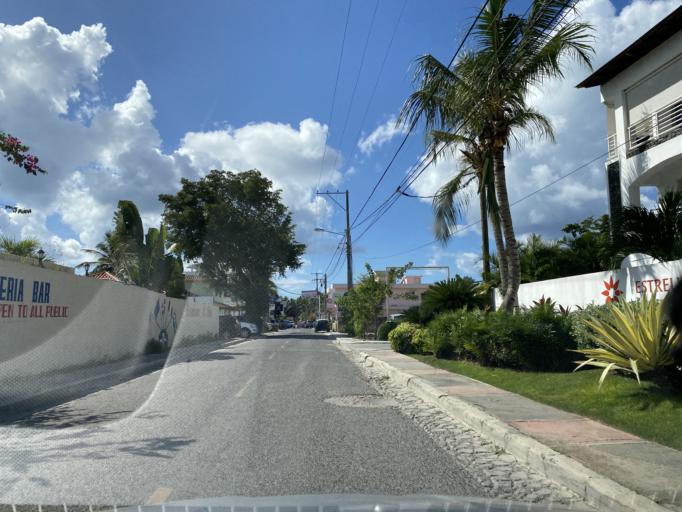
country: DO
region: La Romana
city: La Romana
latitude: 18.3515
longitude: -68.8275
